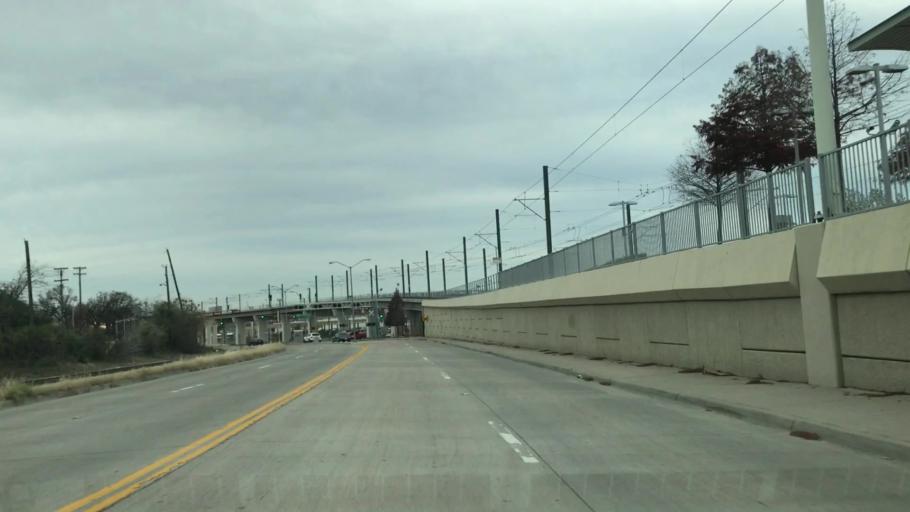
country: US
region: Texas
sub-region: Dallas County
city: Farmers Branch
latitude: 32.8536
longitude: -96.8771
